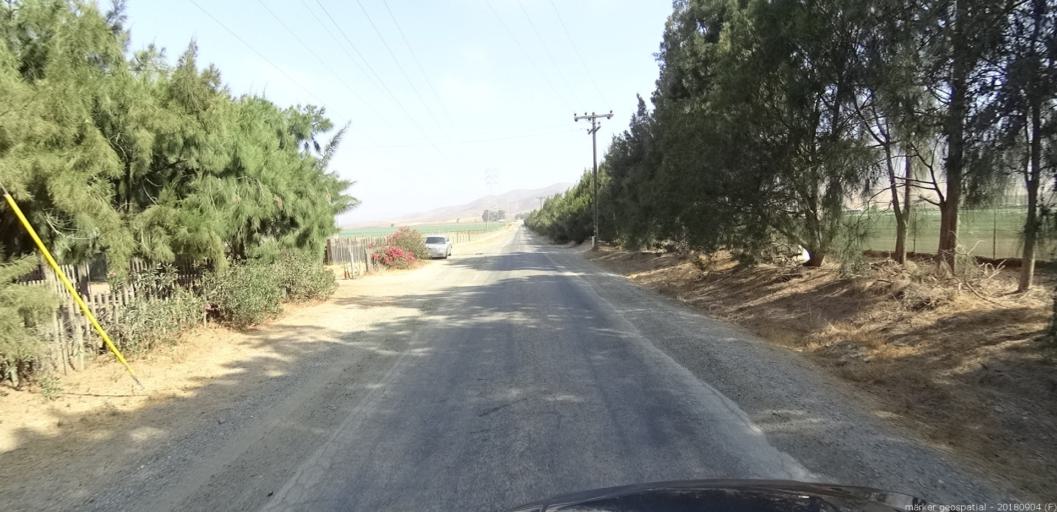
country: US
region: California
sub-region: Monterey County
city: Soledad
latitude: 36.4555
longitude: -121.3318
